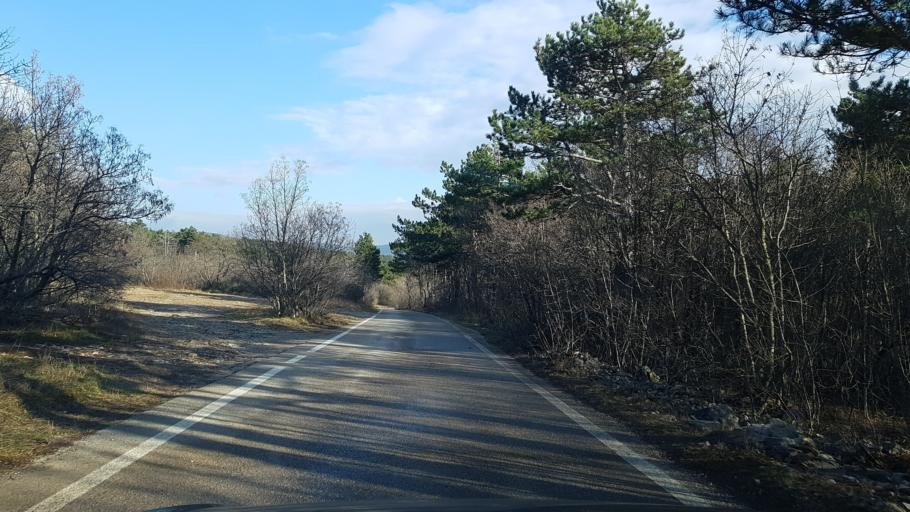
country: IT
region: Friuli Venezia Giulia
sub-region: Provincia di Trieste
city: Dolina
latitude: 45.6292
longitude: 13.8676
